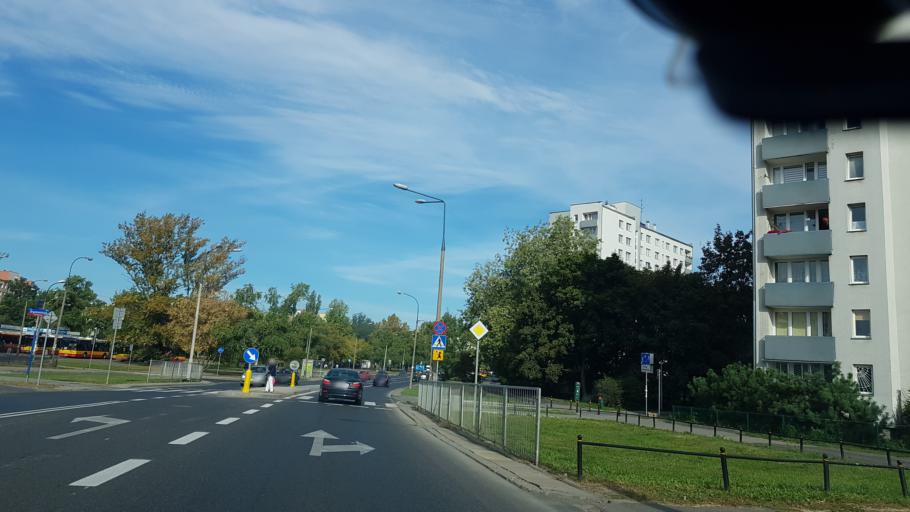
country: PL
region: Masovian Voivodeship
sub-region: Warszawa
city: Bielany
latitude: 52.2721
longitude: 20.9268
